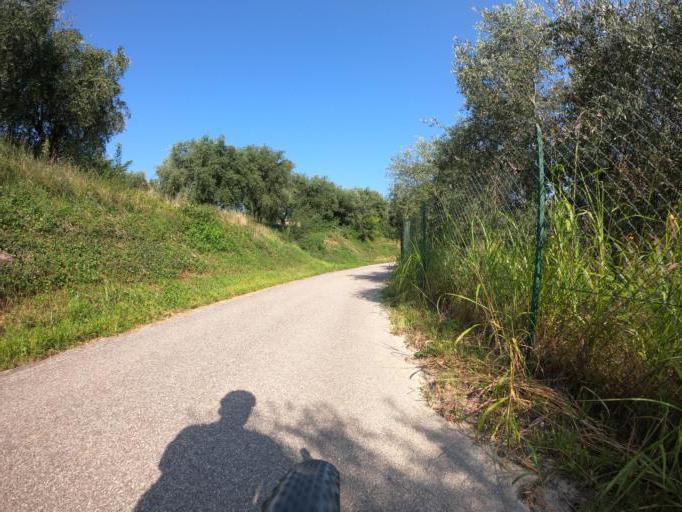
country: IT
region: Veneto
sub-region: Provincia di Verona
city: Calmasino
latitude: 45.5072
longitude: 10.7538
